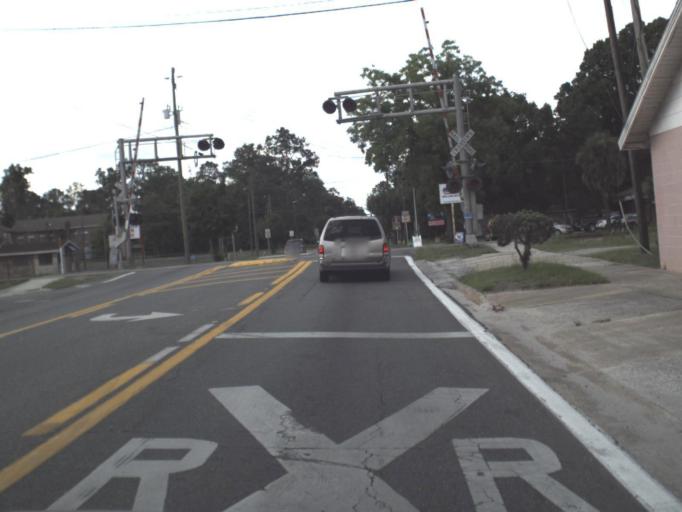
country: US
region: Florida
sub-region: Baker County
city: Macclenny
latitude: 30.2817
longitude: -82.1237
